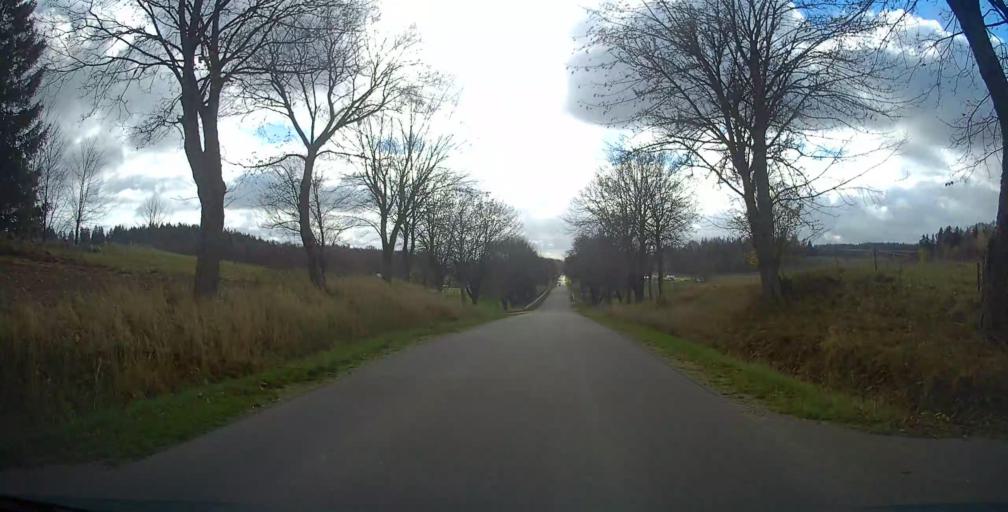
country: PL
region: Podlasie
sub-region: Suwalki
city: Suwalki
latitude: 54.3086
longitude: 22.8805
